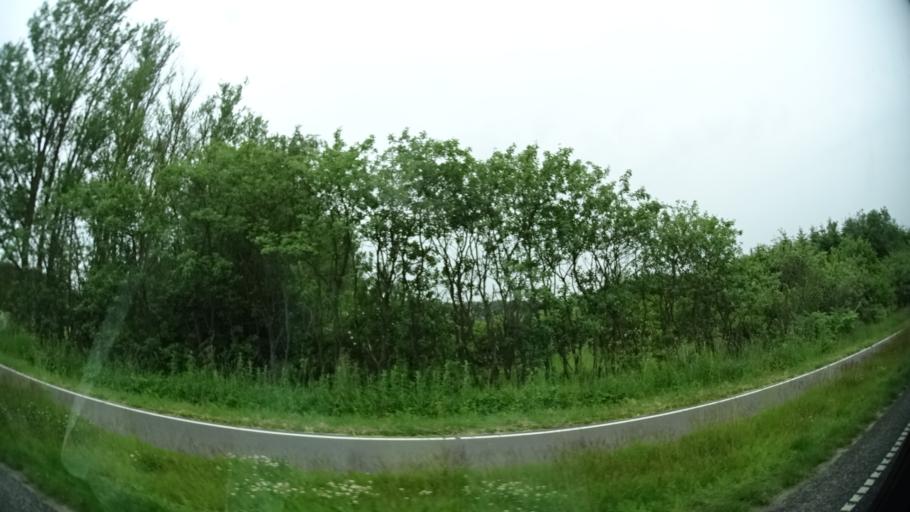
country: DK
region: Central Jutland
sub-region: Arhus Kommune
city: Hjortshoj
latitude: 56.2355
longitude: 10.2971
